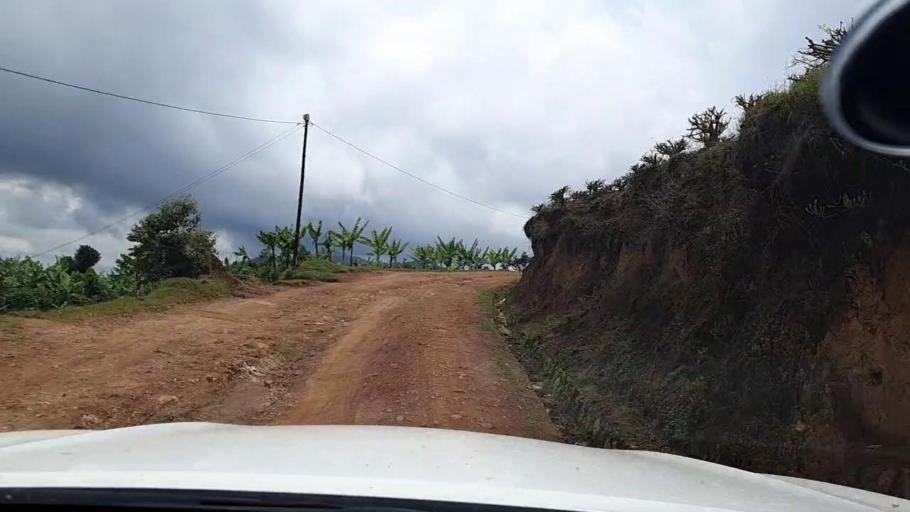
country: RW
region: Western Province
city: Kibuye
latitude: -2.1712
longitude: 29.4333
